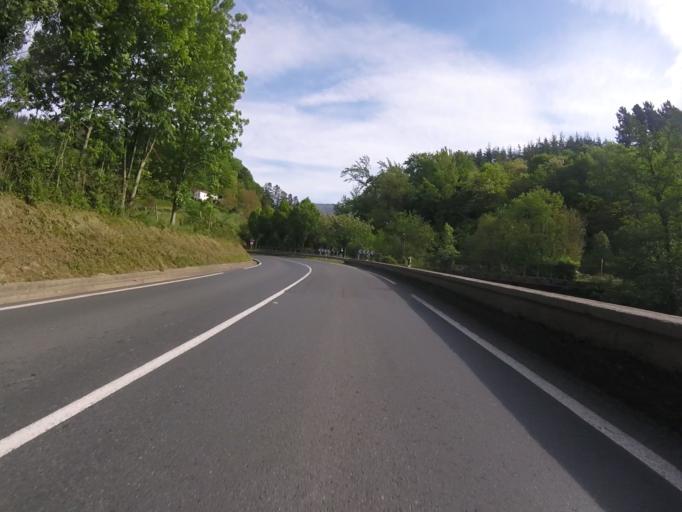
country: ES
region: Basque Country
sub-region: Provincia de Guipuzcoa
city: Urretxu
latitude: 43.1005
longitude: -2.3177
